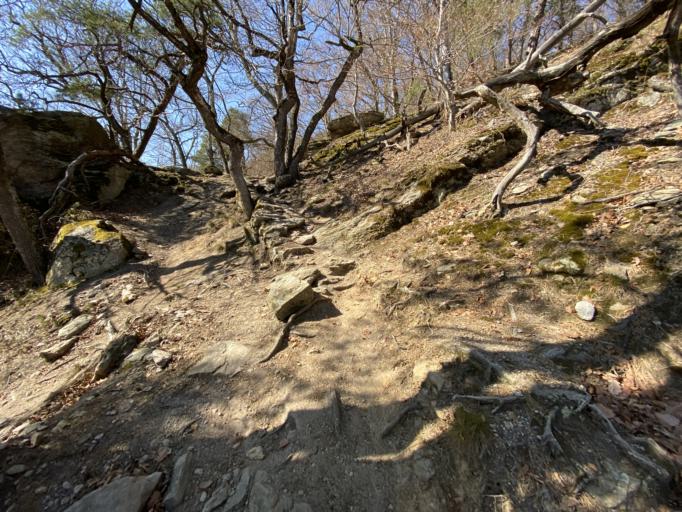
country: AT
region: Lower Austria
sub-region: Politischer Bezirk Krems
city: Durnstein
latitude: 48.4067
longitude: 15.5238
